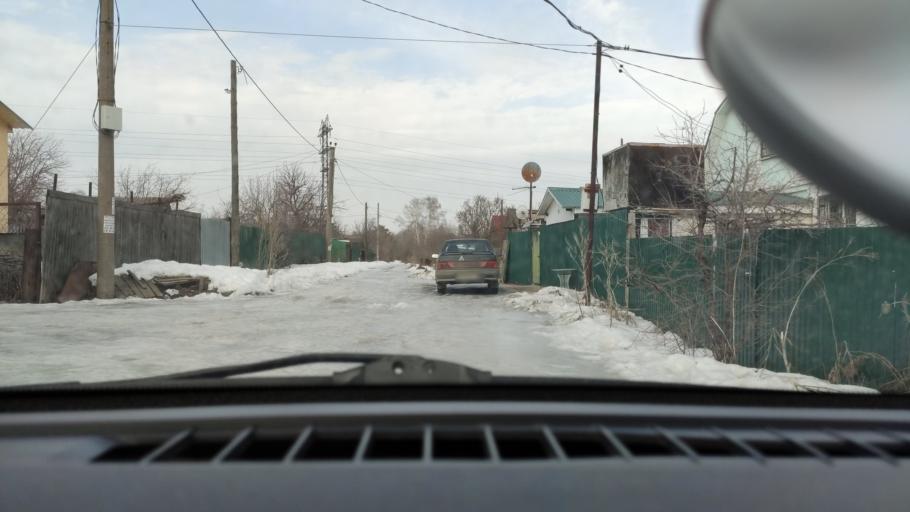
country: RU
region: Samara
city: Petra-Dubrava
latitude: 53.2656
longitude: 50.3058
